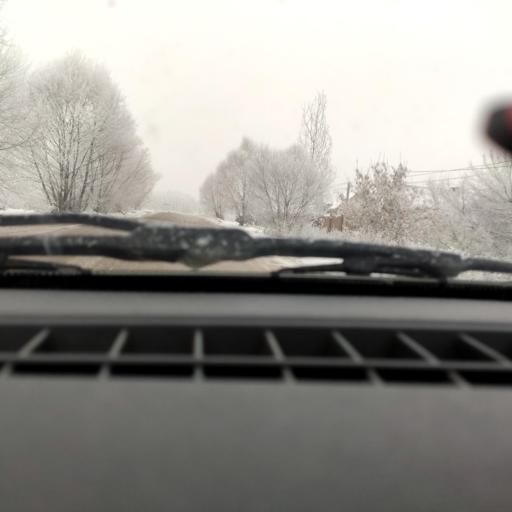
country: RU
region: Bashkortostan
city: Kabakovo
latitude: 54.6985
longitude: 56.1302
